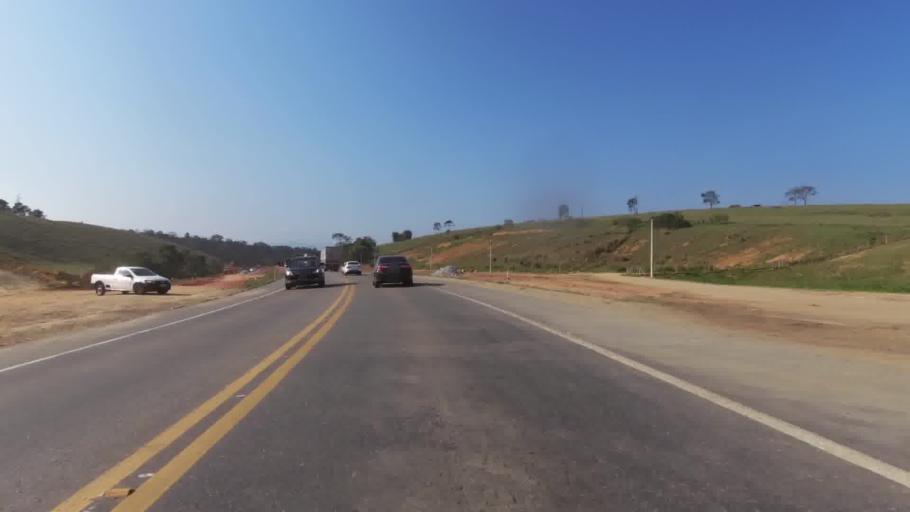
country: BR
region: Espirito Santo
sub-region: Alfredo Chaves
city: Alfredo Chaves
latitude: -20.7272
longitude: -40.7413
